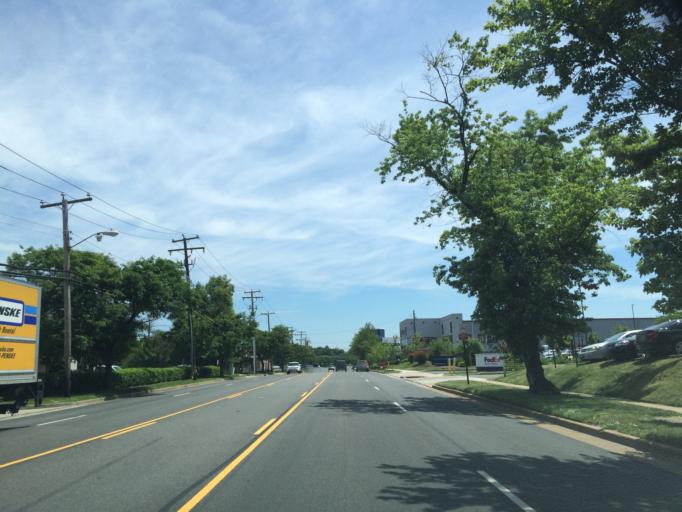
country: US
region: Virginia
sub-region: Fairfax County
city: Rose Hill
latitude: 38.8036
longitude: -77.1172
